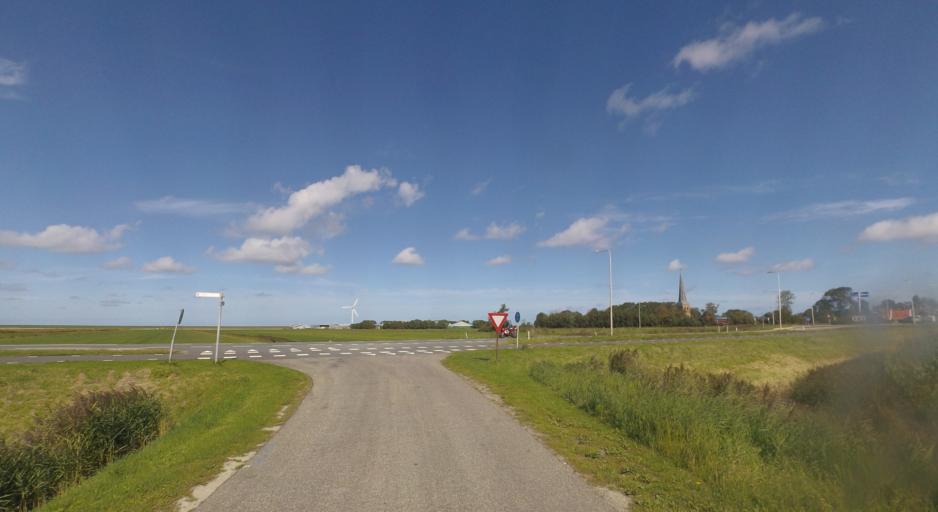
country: NL
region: Friesland
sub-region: Gemeente Dongeradeel
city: Holwerd
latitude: 53.3677
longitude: 5.8940
